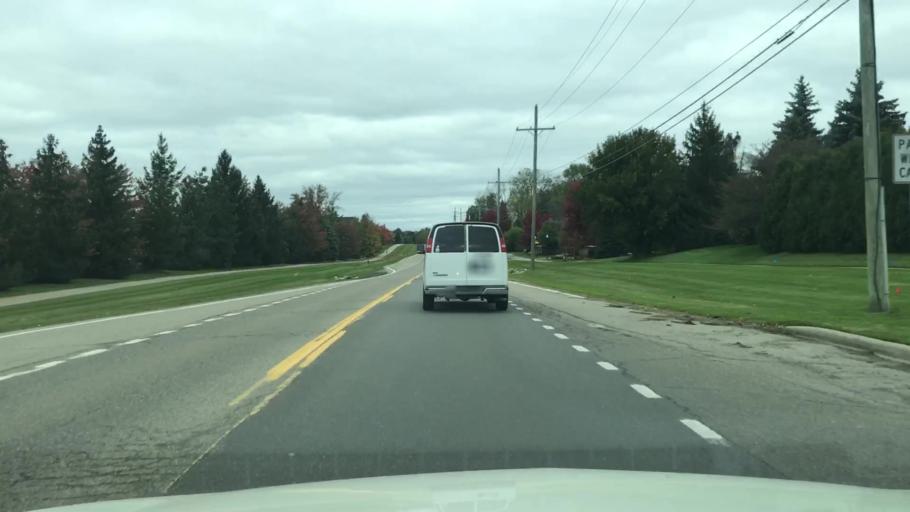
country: US
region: Michigan
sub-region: Oakland County
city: Rochester
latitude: 42.6878
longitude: -83.0944
